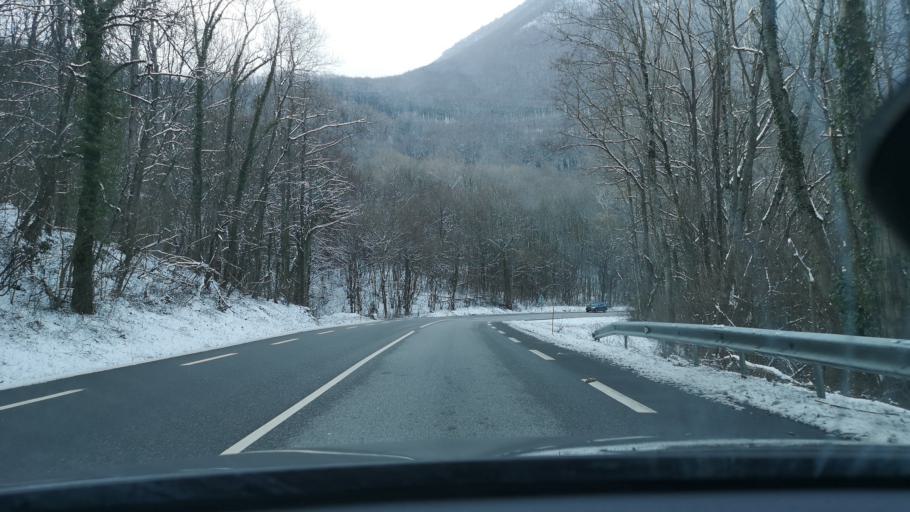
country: FR
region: Rhone-Alpes
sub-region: Departement de l'Ain
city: Collonges
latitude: 46.1079
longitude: 5.8754
